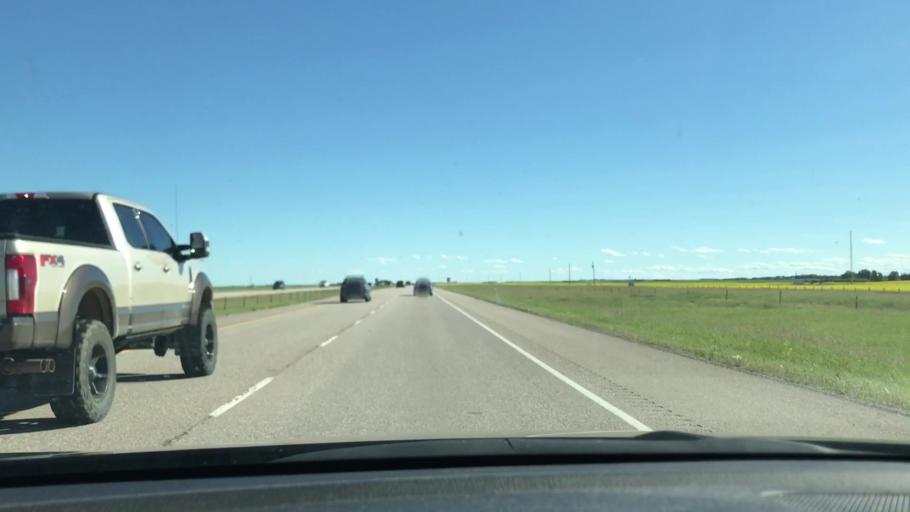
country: CA
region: Alberta
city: Carstairs
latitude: 51.6160
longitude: -114.0255
